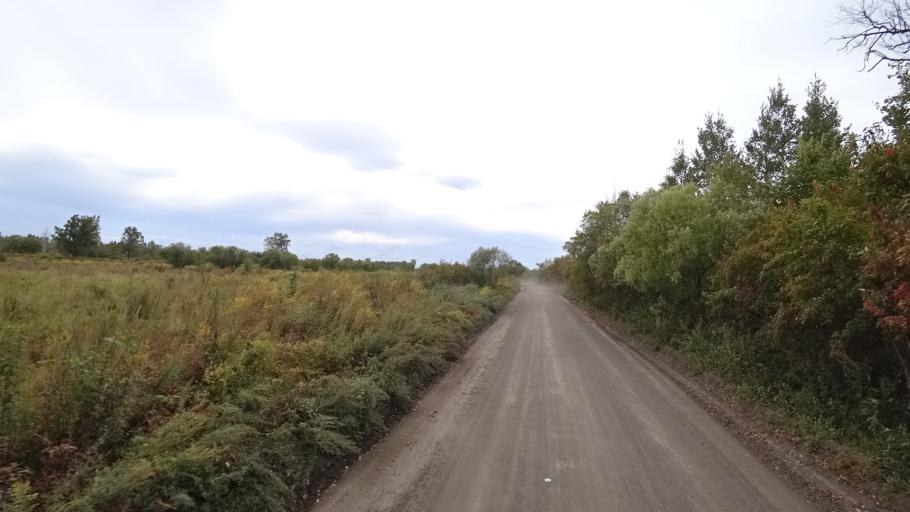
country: RU
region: Amur
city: Arkhara
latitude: 49.3557
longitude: 130.1317
